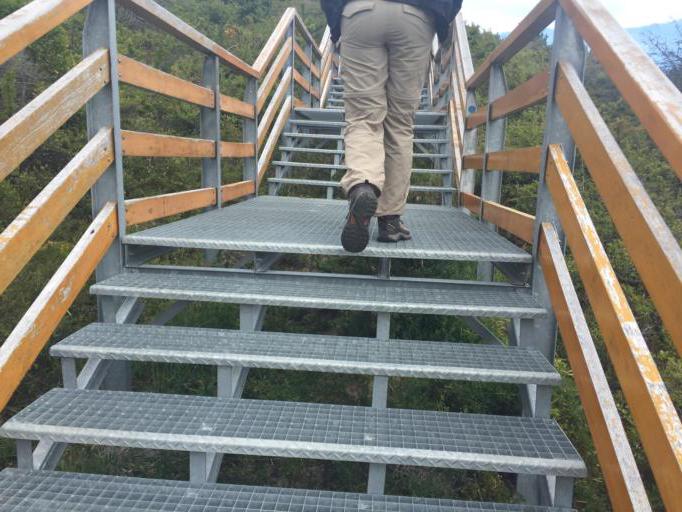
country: AR
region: Santa Cruz
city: El Calafate
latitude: -50.4647
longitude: -73.0339
